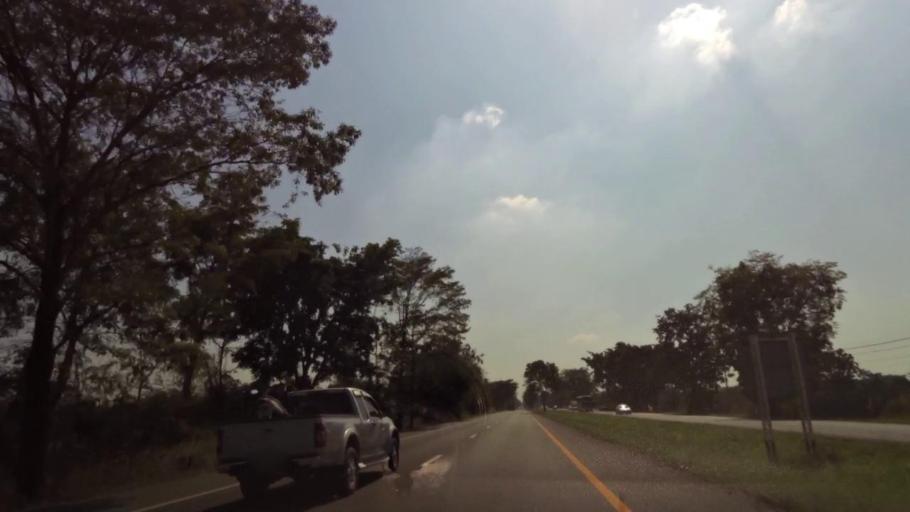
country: TH
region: Phichit
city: Bueng Na Rang
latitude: 16.2252
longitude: 100.1262
